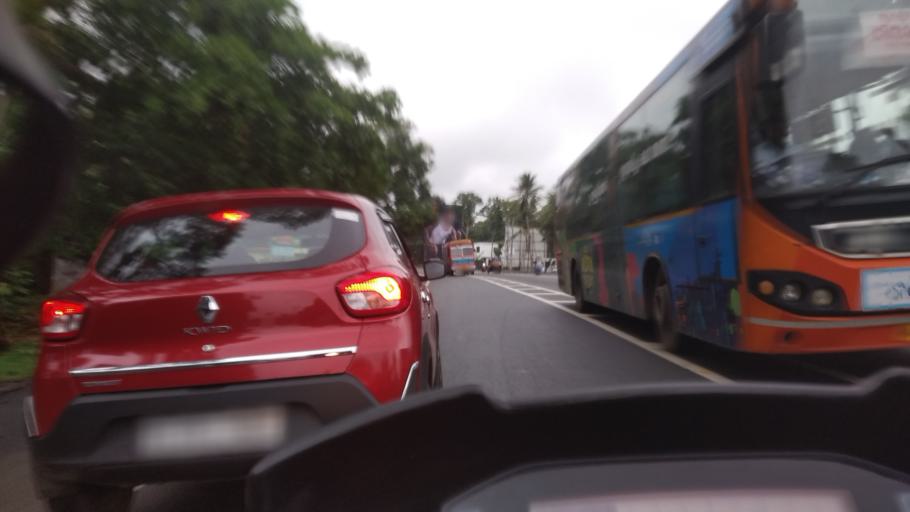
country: IN
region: Kerala
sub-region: Alappuzha
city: Mavelikara
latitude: 9.3188
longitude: 76.4251
